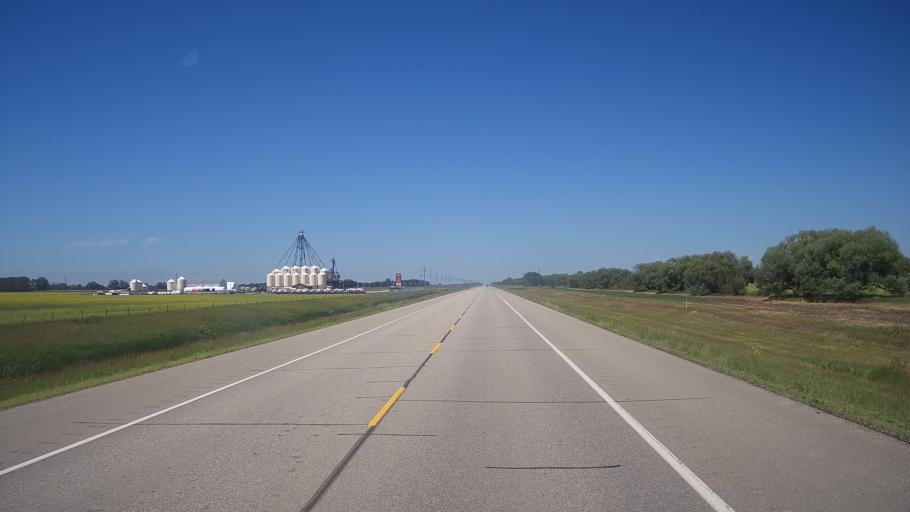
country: CA
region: Manitoba
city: Neepawa
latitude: 50.2257
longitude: -99.0354
